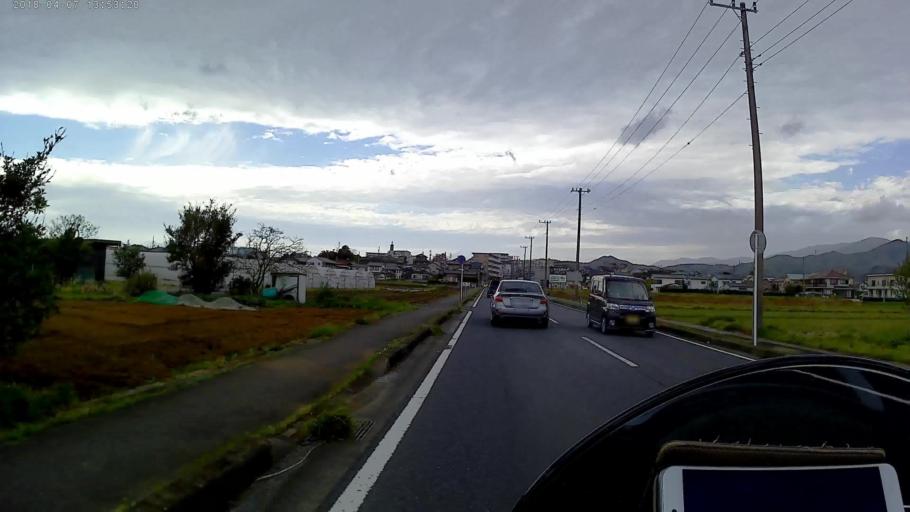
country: JP
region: Kanagawa
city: Isehara
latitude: 35.3673
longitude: 139.2904
